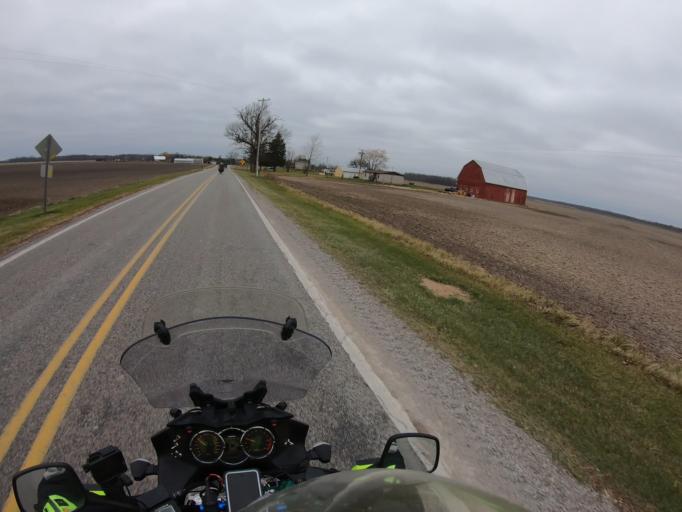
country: US
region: Michigan
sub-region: Saginaw County
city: Saint Charles
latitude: 43.2672
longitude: -84.1121
